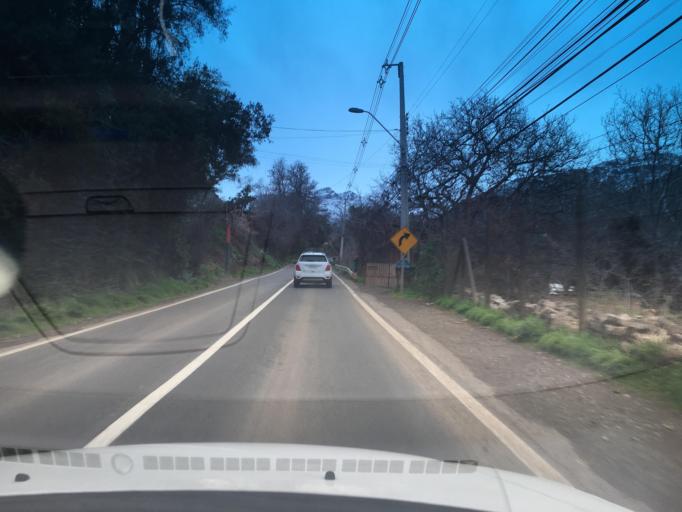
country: CL
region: Santiago Metropolitan
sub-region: Provincia de Cordillera
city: Puente Alto
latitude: -33.6626
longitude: -70.3501
